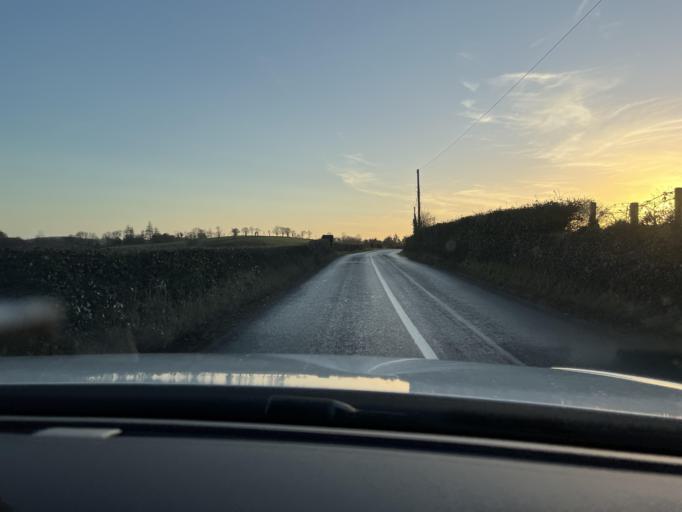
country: IE
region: Ulster
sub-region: An Cabhan
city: Ballyconnell
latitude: 54.0610
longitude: -7.6896
